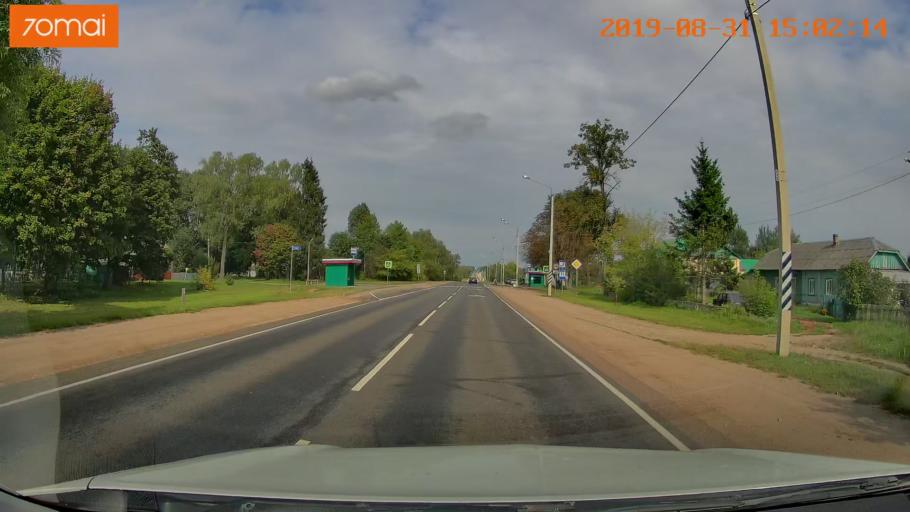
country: RU
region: Kaluga
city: Spas-Demensk
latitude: 54.3444
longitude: 34.0712
